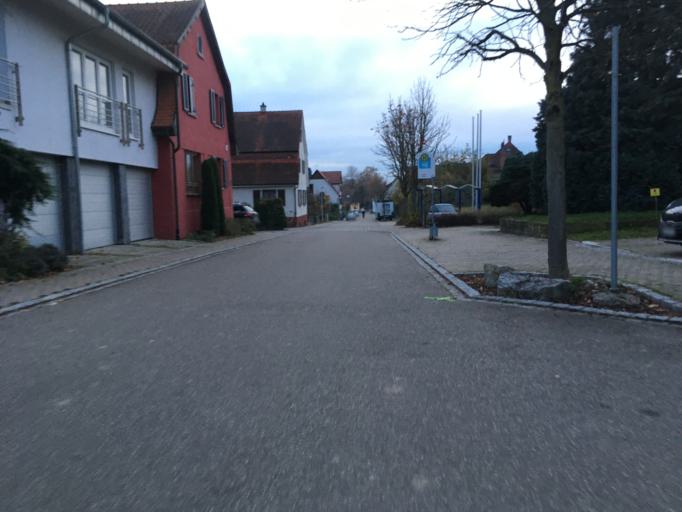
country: DE
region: Baden-Wuerttemberg
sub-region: Regierungsbezirk Stuttgart
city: Abstatt
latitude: 49.0694
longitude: 9.2890
